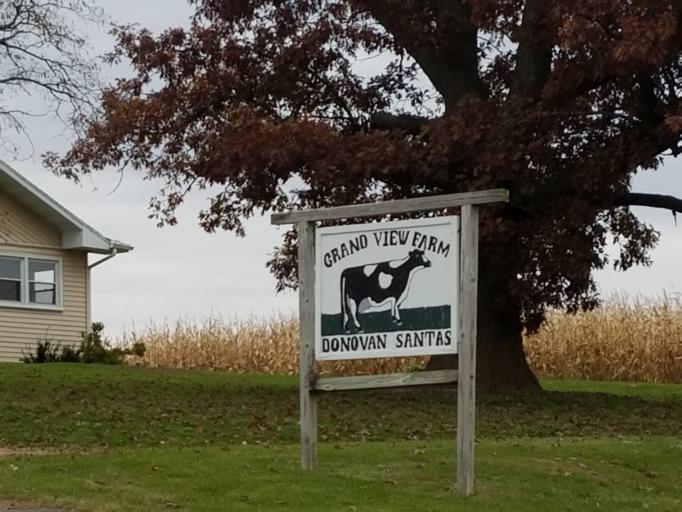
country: US
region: Wisconsin
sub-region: Vernon County
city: Hillsboro
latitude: 43.6511
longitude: -90.2942
